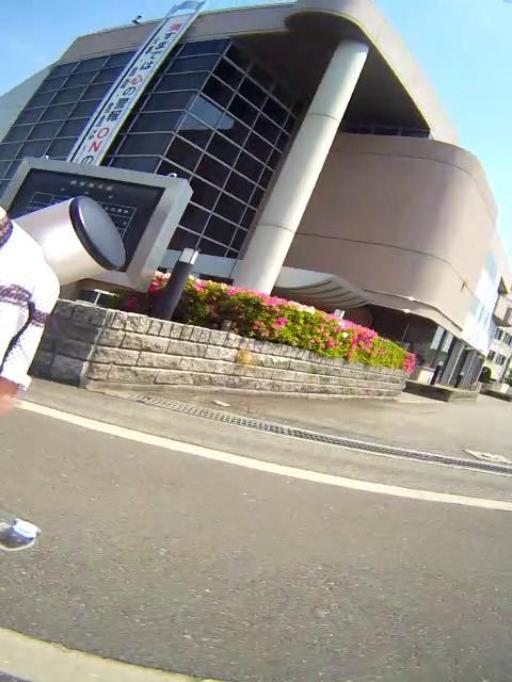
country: JP
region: Osaka
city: Matsubara
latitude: 34.5370
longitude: 135.5617
